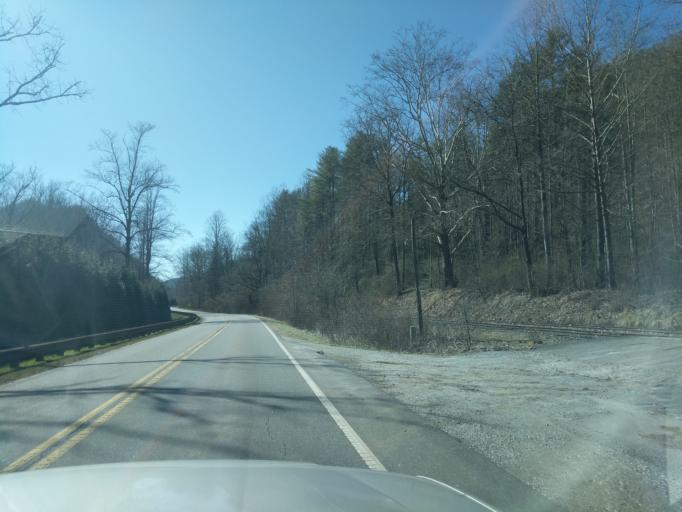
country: US
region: North Carolina
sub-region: Graham County
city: Robbinsville
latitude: 35.2907
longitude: -83.6637
